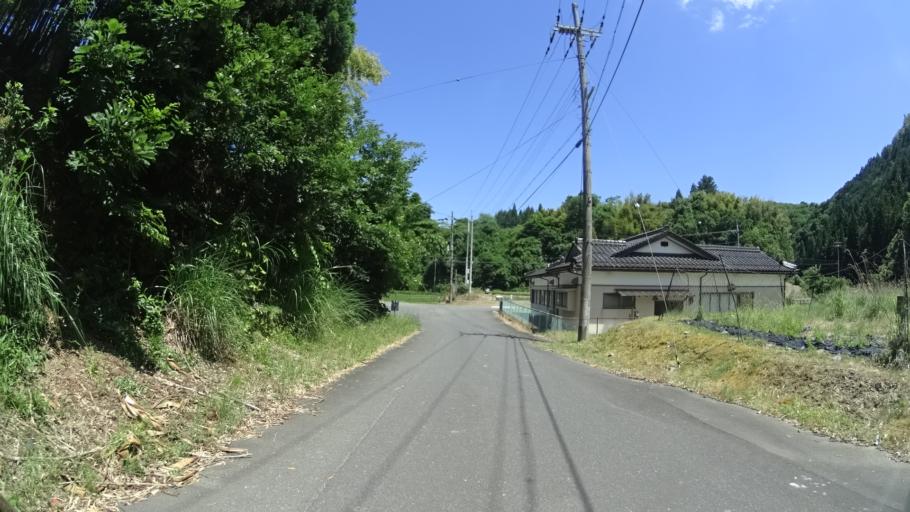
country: JP
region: Kyoto
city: Miyazu
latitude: 35.4407
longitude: 135.1878
